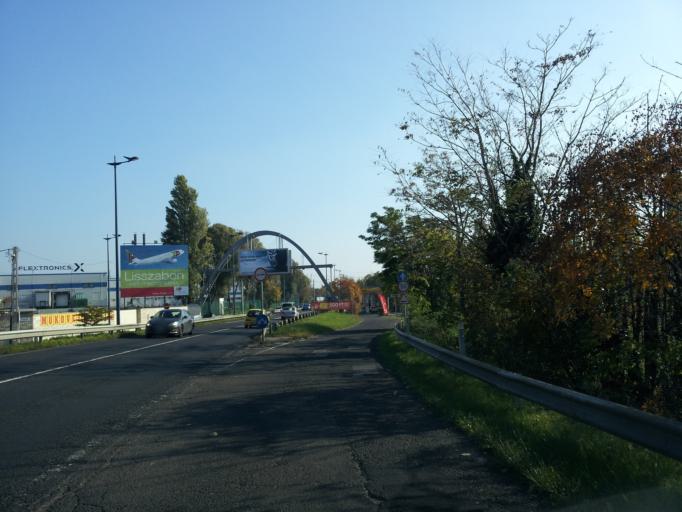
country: HU
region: Budapest
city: Budapest XVIII. keruelet
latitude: 47.4618
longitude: 19.1683
